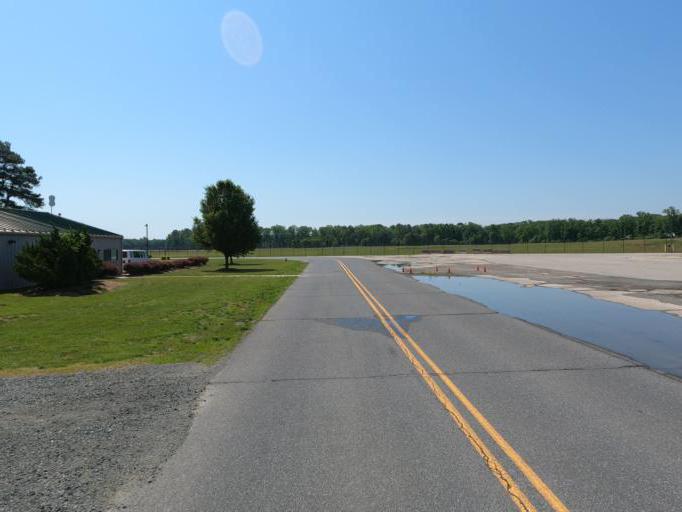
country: US
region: Delaware
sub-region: Sussex County
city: Georgetown
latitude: 38.6868
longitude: -75.3510
